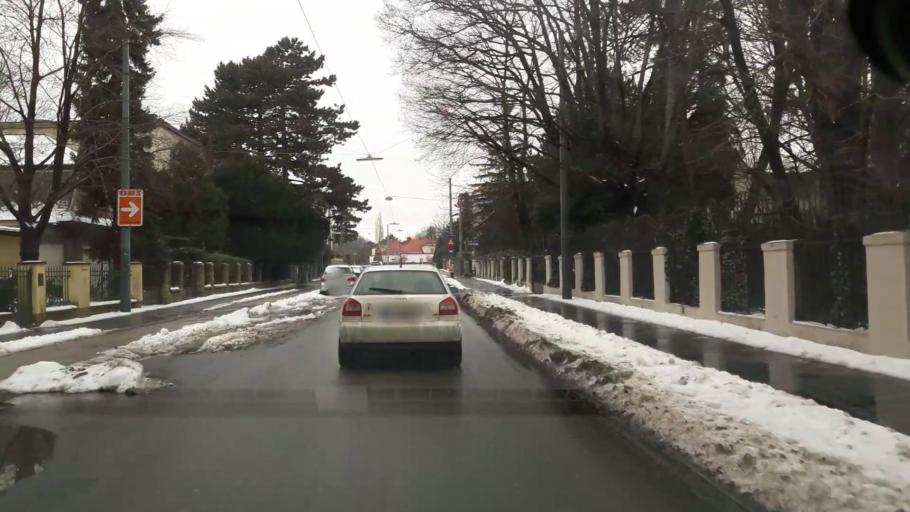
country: AT
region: Lower Austria
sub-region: Politischer Bezirk Modling
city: Perchtoldsdorf
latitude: 48.1826
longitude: 16.2833
